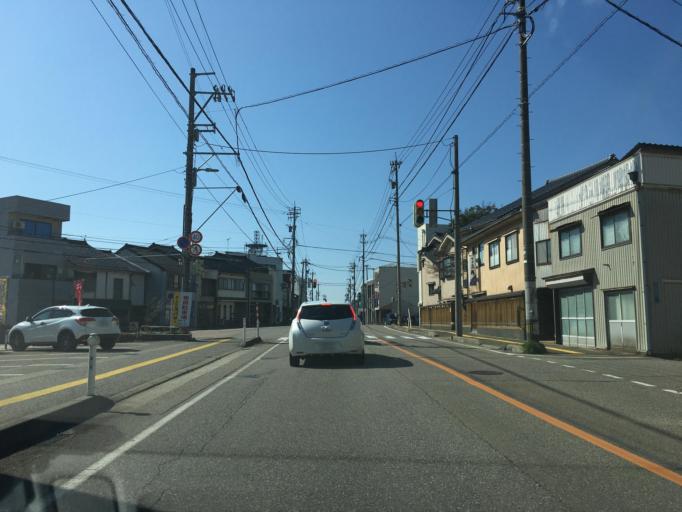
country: JP
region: Toyama
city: Nishishinminato
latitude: 36.7790
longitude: 137.0867
